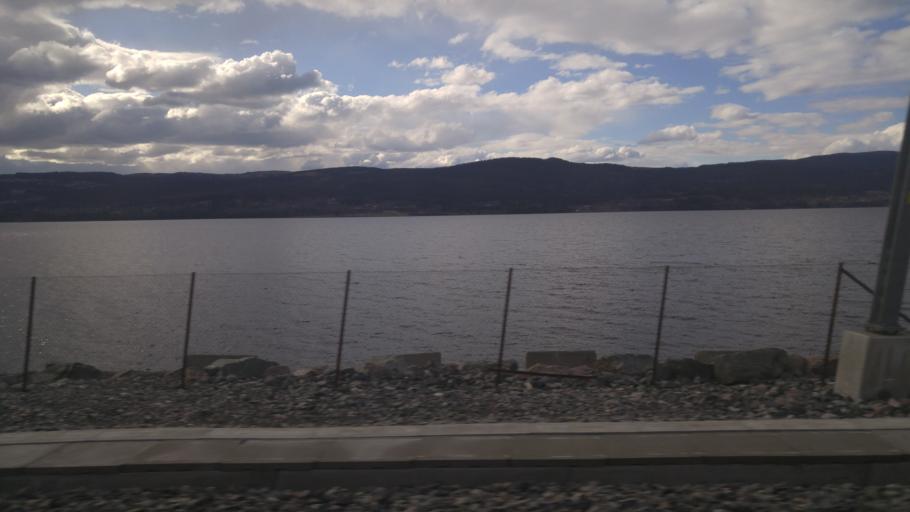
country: NO
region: Akershus
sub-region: Eidsvoll
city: Eidsvoll
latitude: 60.5059
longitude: 11.2398
